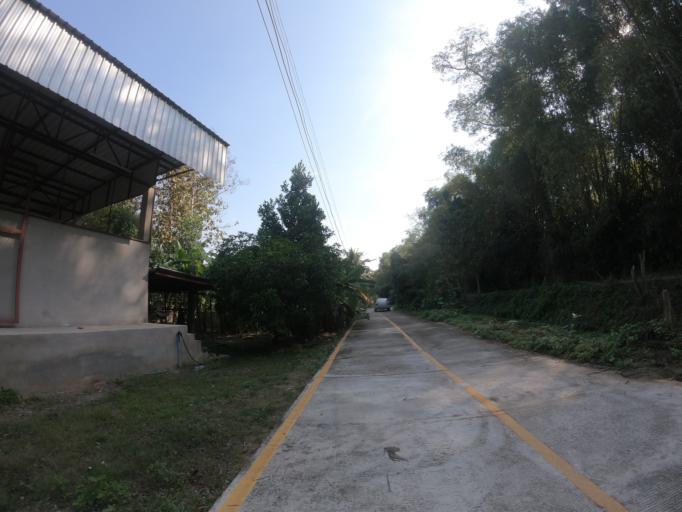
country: TH
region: Chiang Mai
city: Chiang Mai
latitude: 18.7396
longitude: 98.9839
